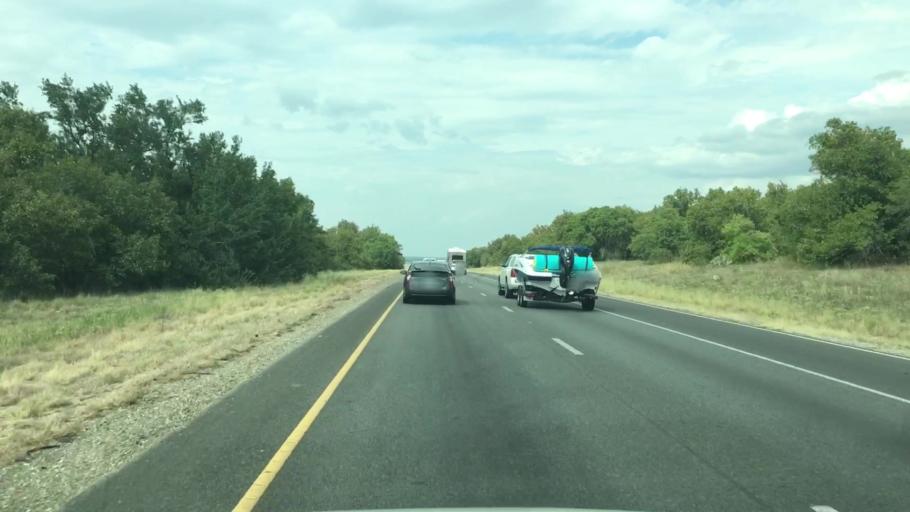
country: US
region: Texas
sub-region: Bexar County
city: Elmendorf
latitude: 29.1938
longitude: -98.4218
